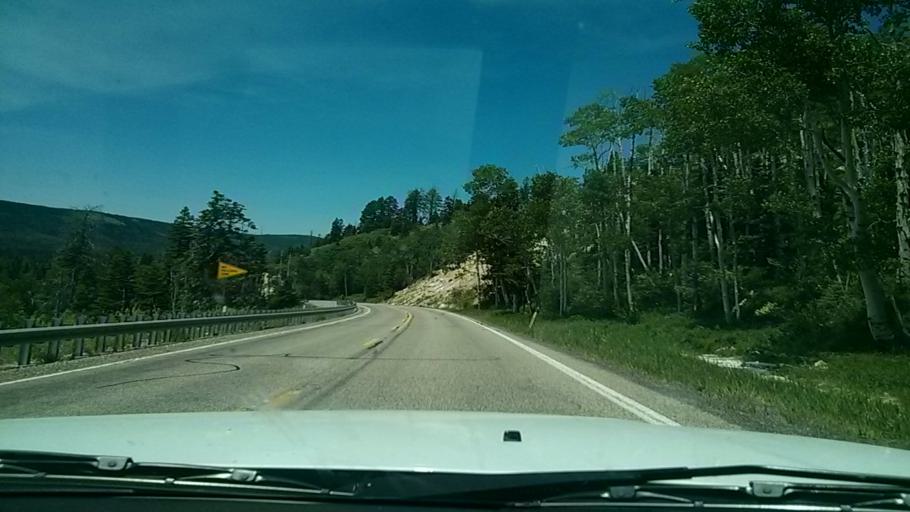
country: US
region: Utah
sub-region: Iron County
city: Cedar City
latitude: 37.5932
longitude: -112.8854
